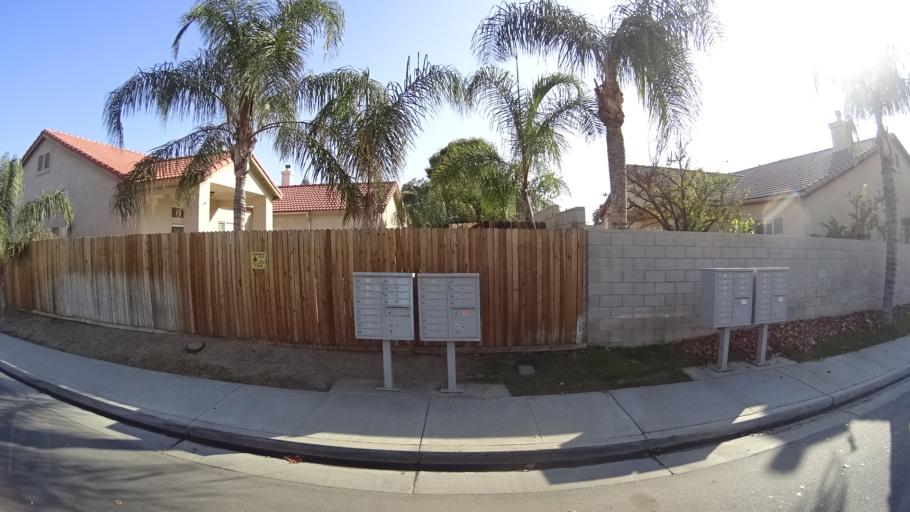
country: US
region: California
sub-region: Kern County
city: Greenacres
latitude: 35.3640
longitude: -119.1122
